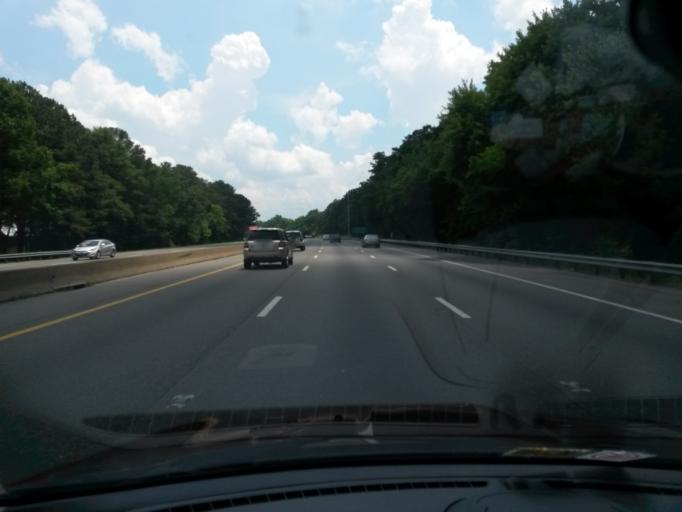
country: US
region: Virginia
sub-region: Chesterfield County
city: Bellwood
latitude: 37.3886
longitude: -77.4209
